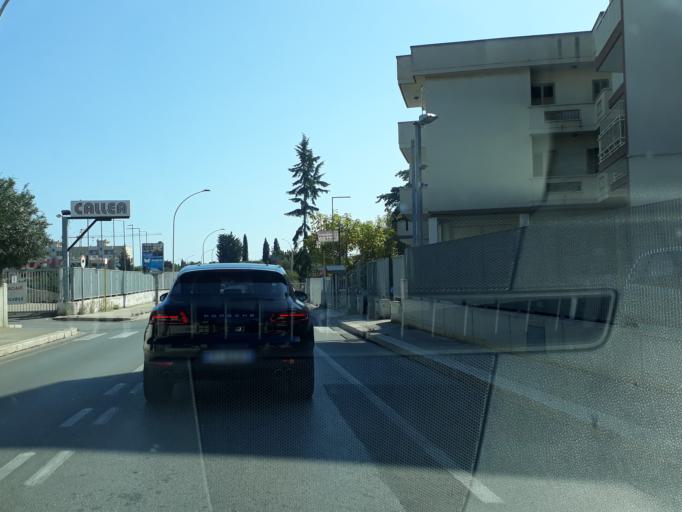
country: IT
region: Apulia
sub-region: Provincia di Bari
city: Monopoli
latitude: 40.9471
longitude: 17.2927
